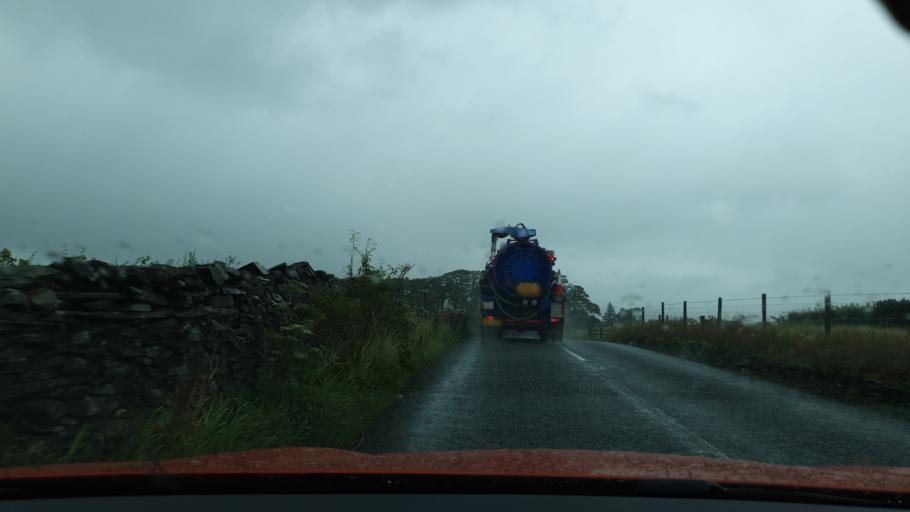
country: GB
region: England
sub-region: Cumbria
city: Millom
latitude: 54.2738
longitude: -3.2221
